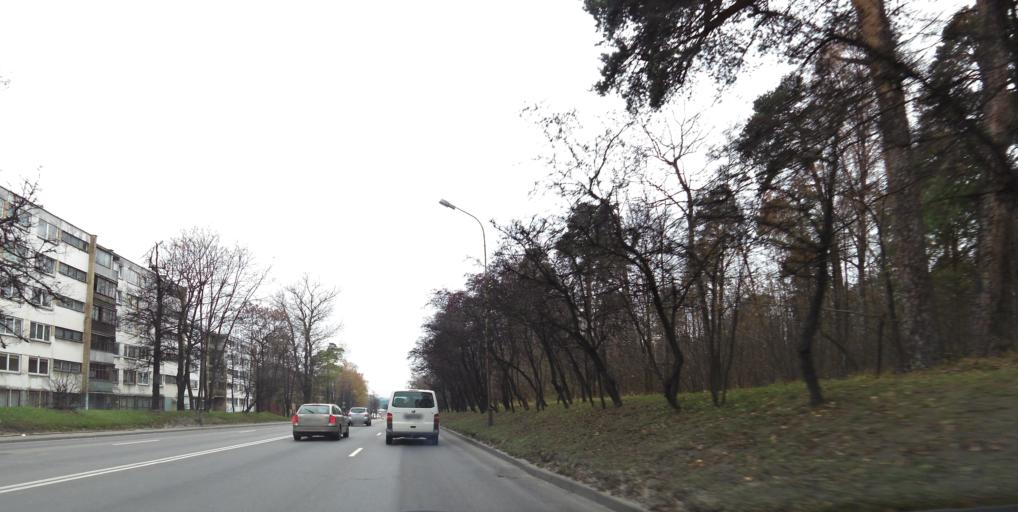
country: LT
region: Vilnius County
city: Vilkpede
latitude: 54.6752
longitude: 25.2437
